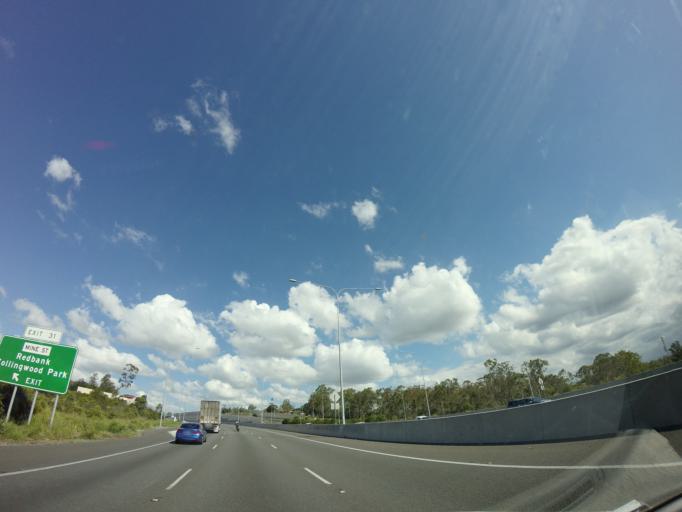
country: AU
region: Queensland
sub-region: Ipswich
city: Redbank
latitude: -27.6032
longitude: 152.8613
